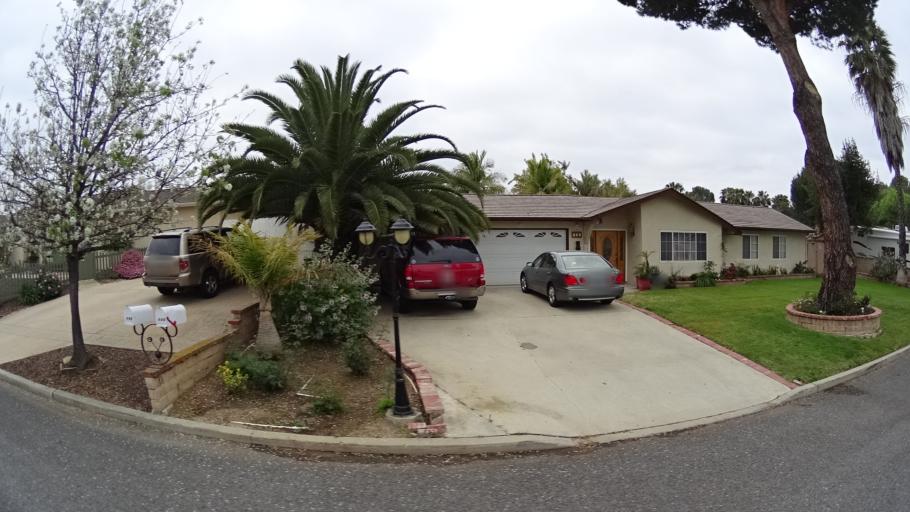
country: US
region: California
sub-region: Ventura County
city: Thousand Oaks
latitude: 34.2068
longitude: -118.8661
